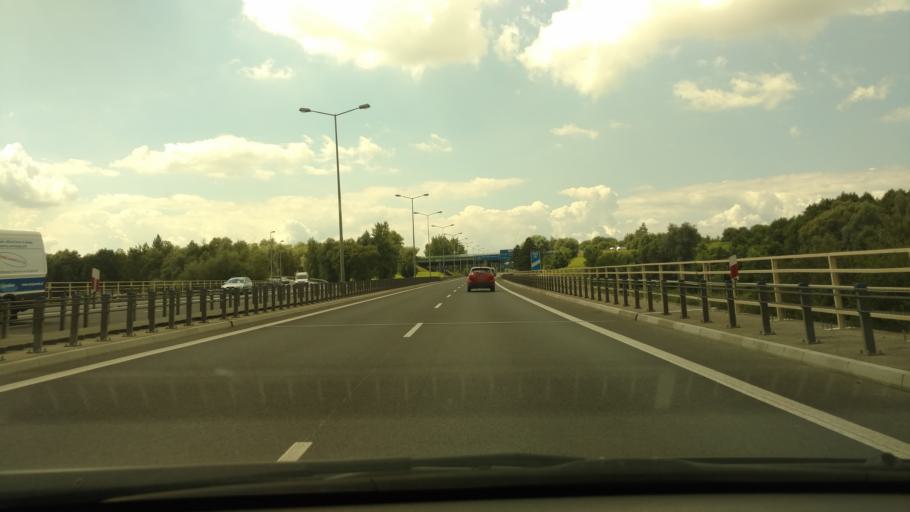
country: PL
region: Lesser Poland Voivodeship
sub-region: Powiat krakowski
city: Balice
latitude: 50.0889
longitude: 19.8090
